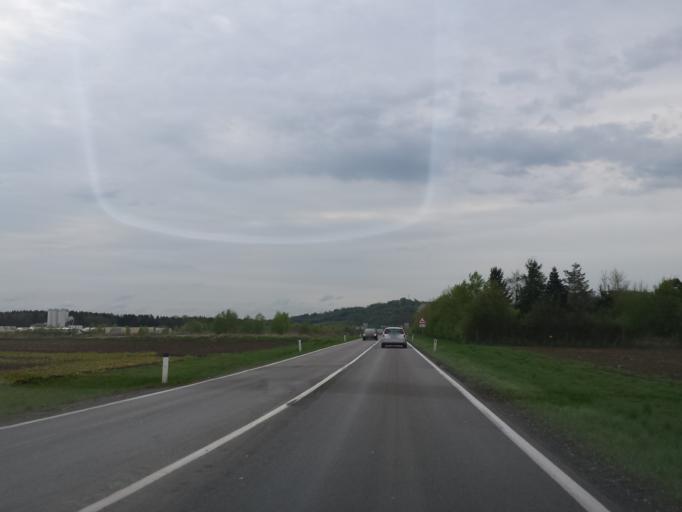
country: AT
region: Styria
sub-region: Politischer Bezirk Hartberg-Fuerstenfeld
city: Soechau
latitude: 47.0736
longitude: 16.0030
